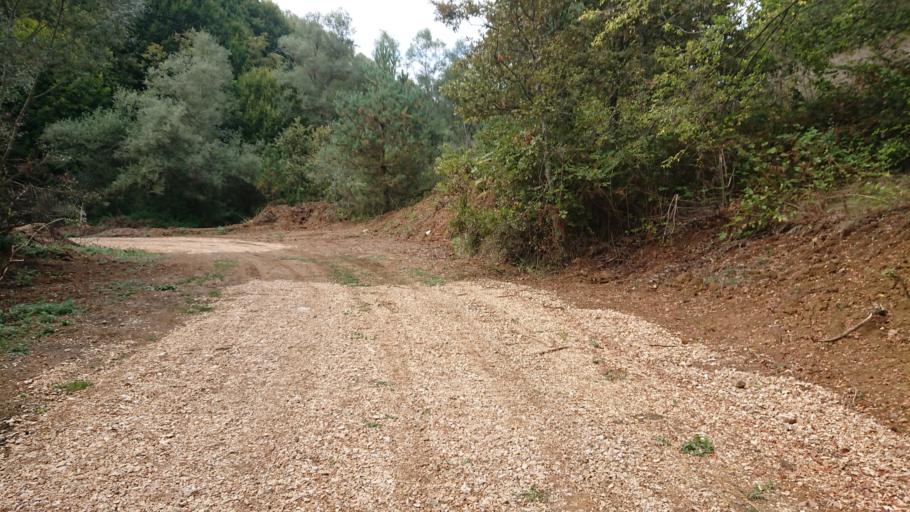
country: TR
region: Bilecik
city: Pazaryeri
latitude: 40.0191
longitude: 29.7898
